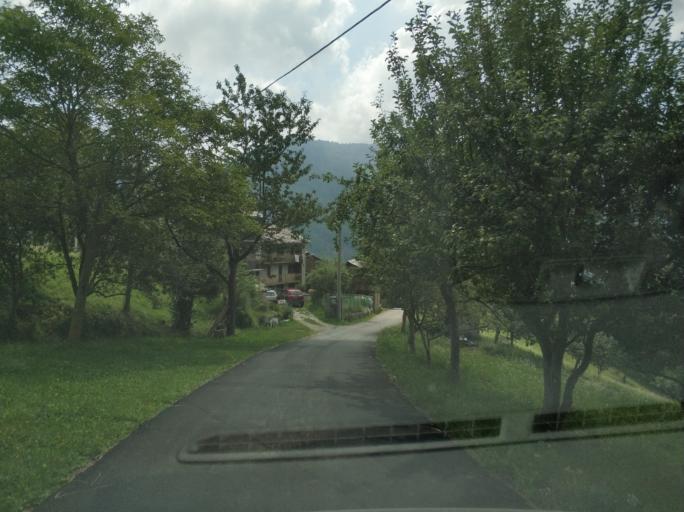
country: IT
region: Piedmont
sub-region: Provincia di Torino
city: Viu
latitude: 45.1995
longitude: 7.3809
